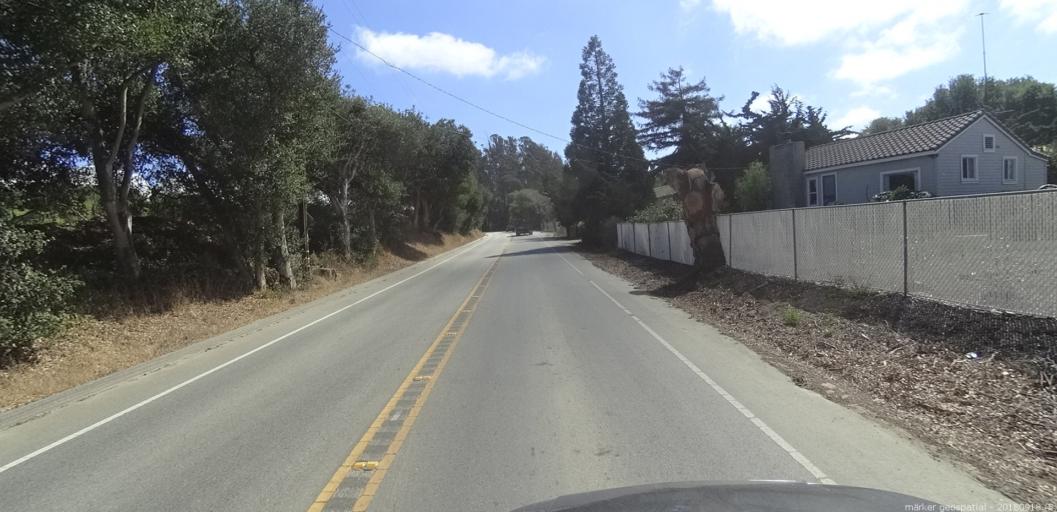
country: US
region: California
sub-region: Monterey County
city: Prunedale
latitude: 36.7771
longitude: -121.6909
